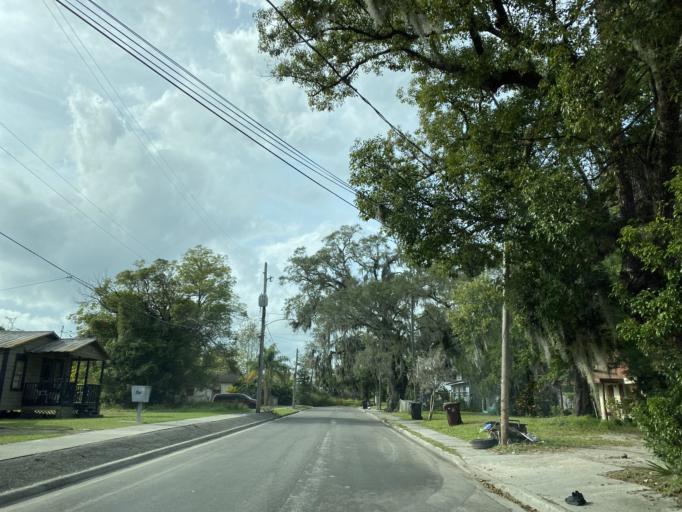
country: US
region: Florida
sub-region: Orange County
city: Orlando
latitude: 28.5466
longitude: -81.3937
